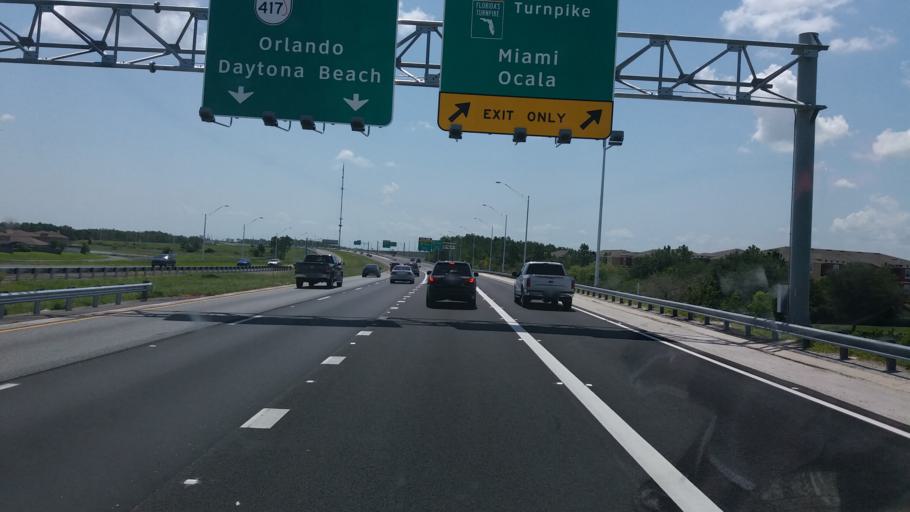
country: US
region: Florida
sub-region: Orange County
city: Hunters Creek
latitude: 28.3698
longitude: -81.3977
